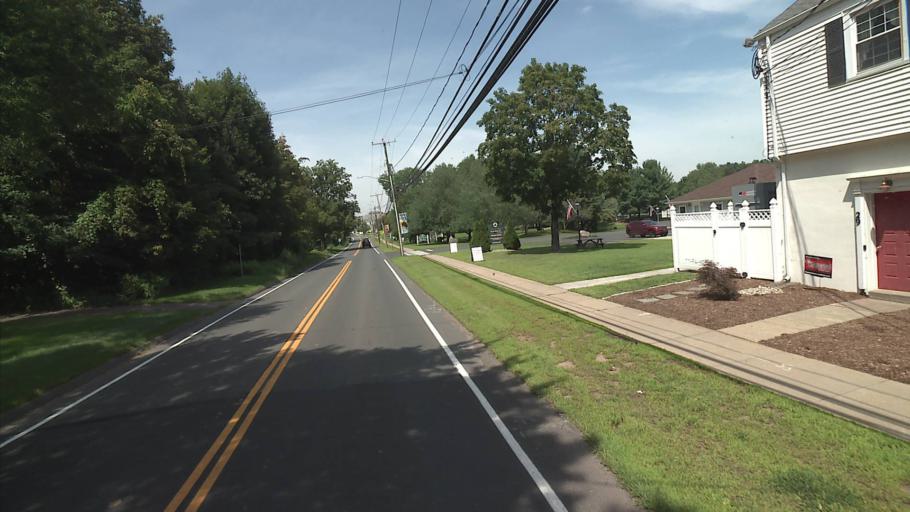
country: US
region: Connecticut
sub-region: Tolland County
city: Ellington
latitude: 41.9024
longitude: -72.4639
